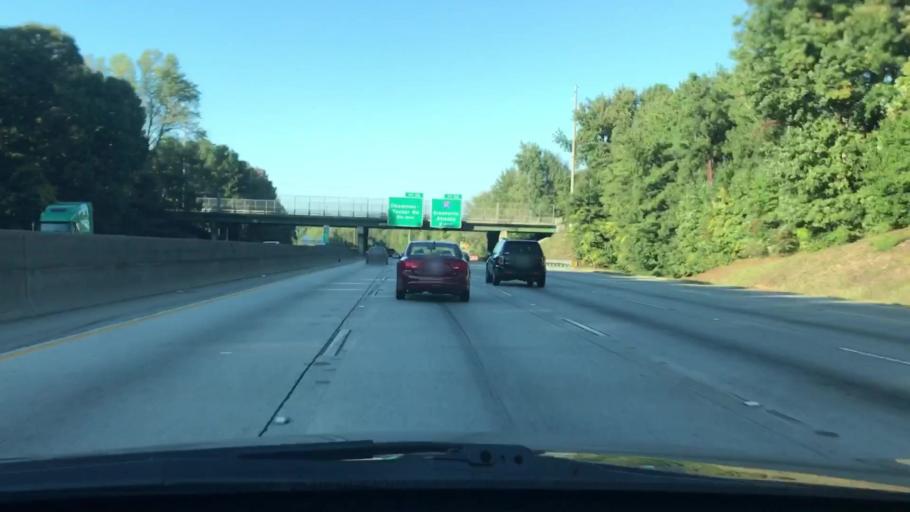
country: US
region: Georgia
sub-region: DeKalb County
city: Tucker
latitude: 33.8499
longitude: -84.2467
